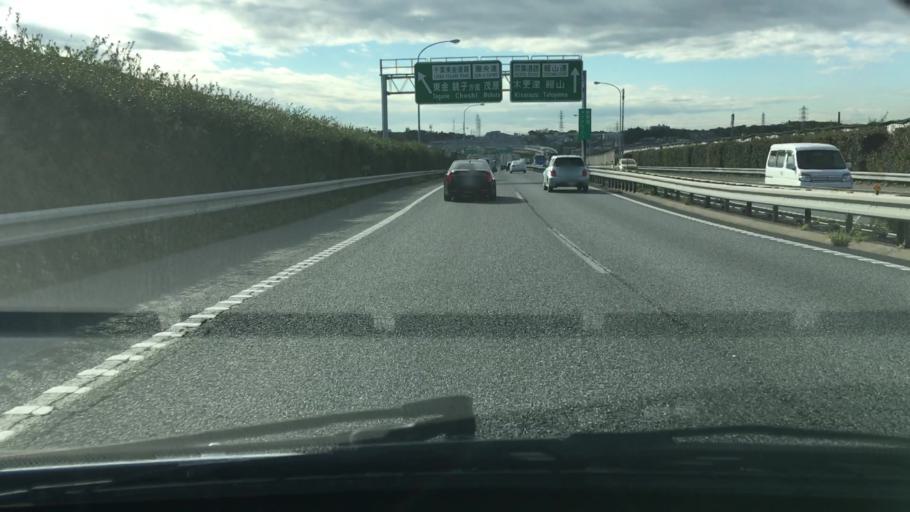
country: JP
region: Chiba
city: Chiba
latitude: 35.6097
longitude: 140.1529
